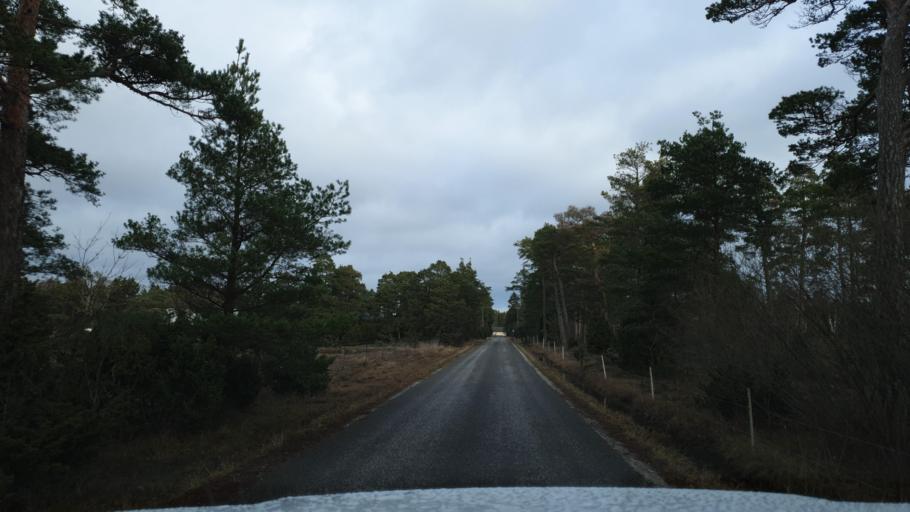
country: SE
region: Gotland
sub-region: Gotland
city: Slite
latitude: 57.3804
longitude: 18.8056
